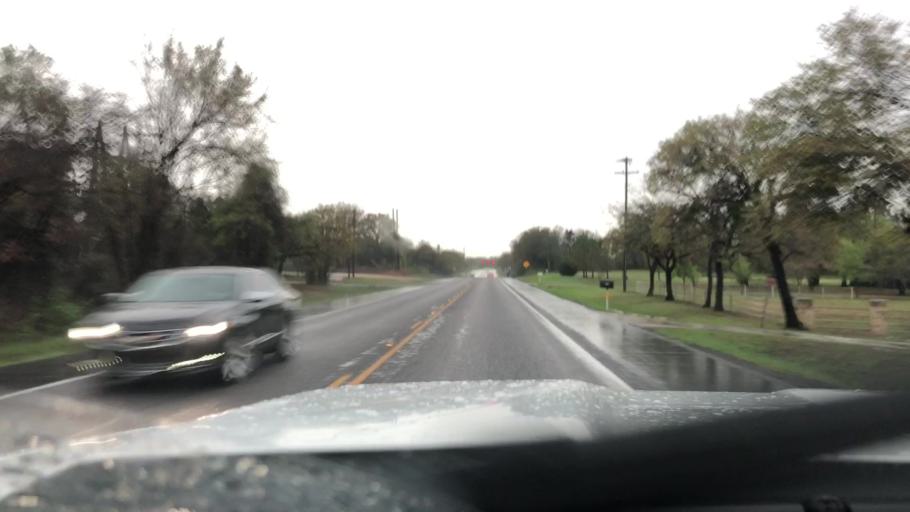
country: US
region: Texas
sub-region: Johnson County
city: Keene
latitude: 32.4136
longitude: -97.3222
